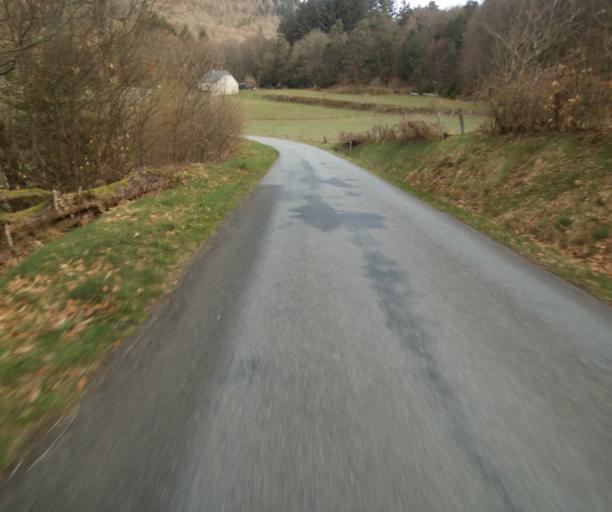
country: FR
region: Limousin
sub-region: Departement de la Correze
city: Correze
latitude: 45.4190
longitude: 1.8978
